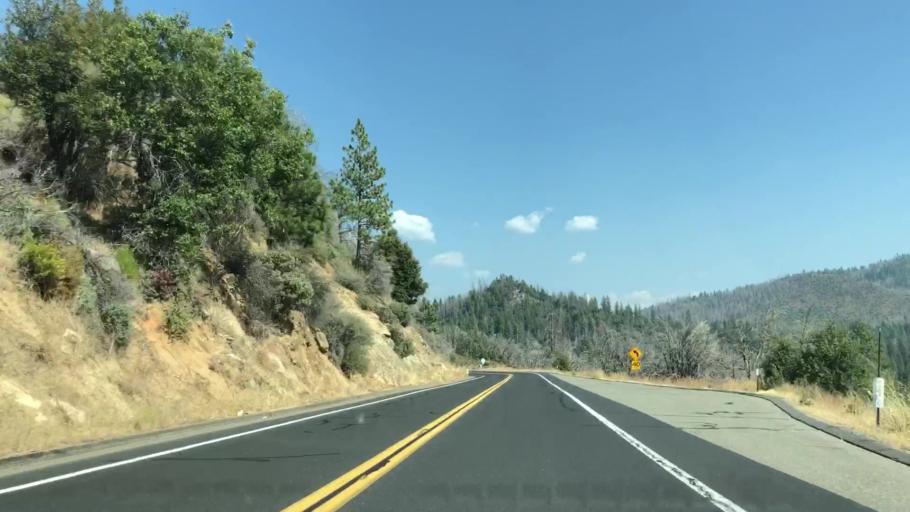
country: US
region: California
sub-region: Mariposa County
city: Midpines
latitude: 37.8155
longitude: -119.9357
